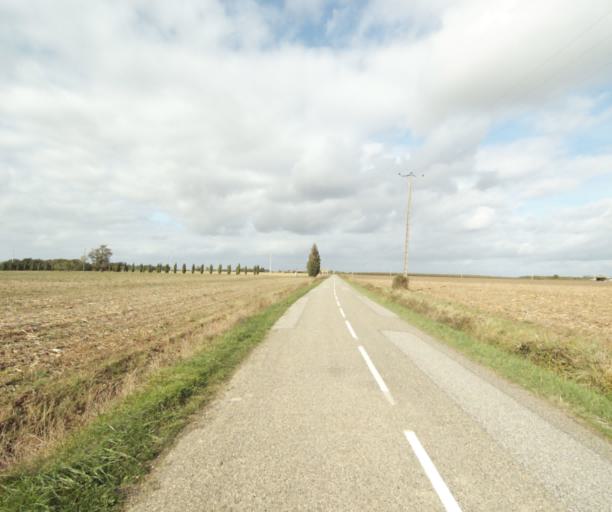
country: FR
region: Midi-Pyrenees
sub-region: Departement du Tarn-et-Garonne
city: Finhan
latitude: 43.9041
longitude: 1.1465
